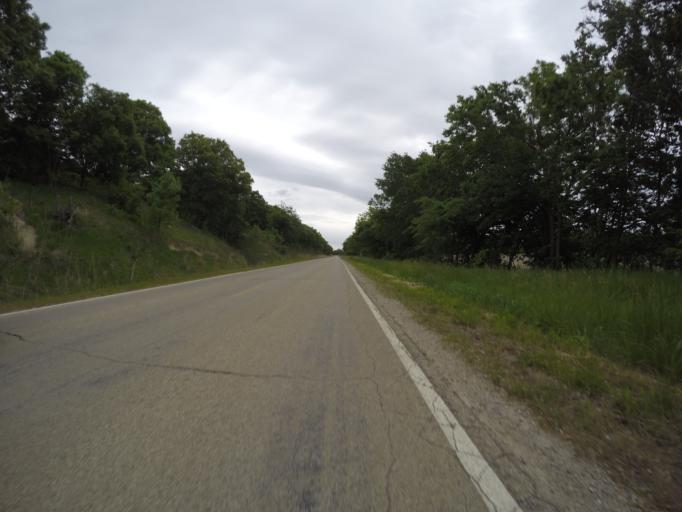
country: US
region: Kansas
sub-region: Pottawatomie County
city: Wamego
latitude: 39.1850
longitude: -96.3419
